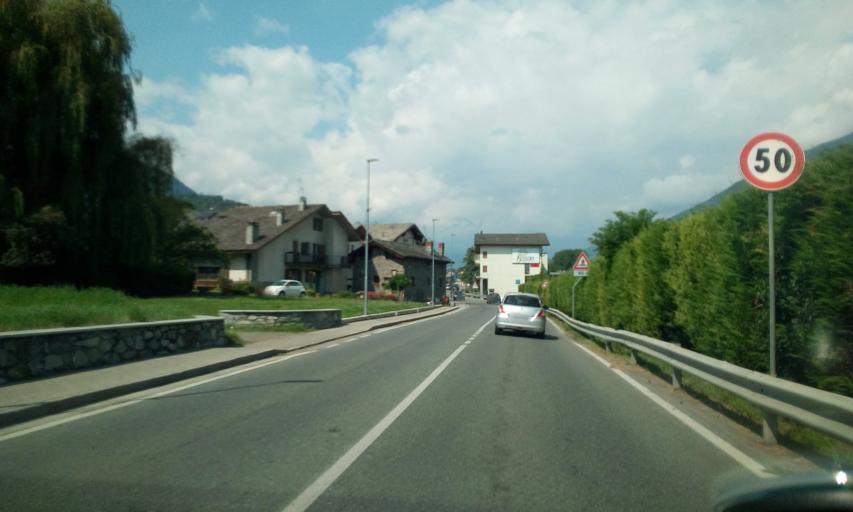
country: IT
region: Aosta Valley
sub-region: Valle d'Aosta
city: Aosta
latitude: 45.7263
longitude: 7.3077
